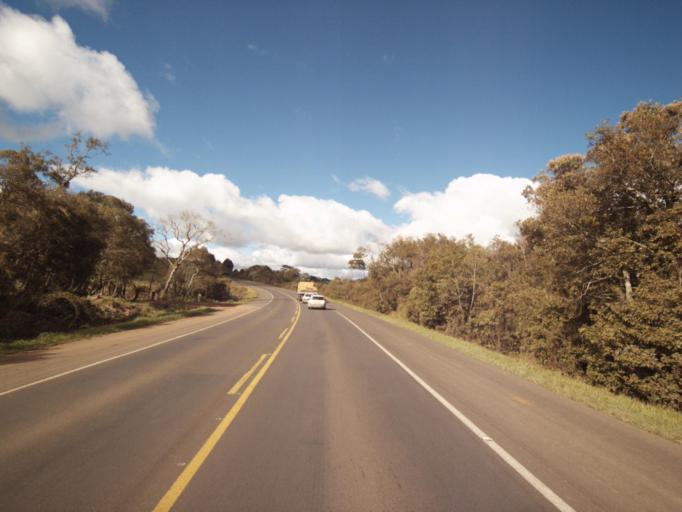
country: BR
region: Santa Catarina
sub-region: Concordia
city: Concordia
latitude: -26.9813
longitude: -51.8148
